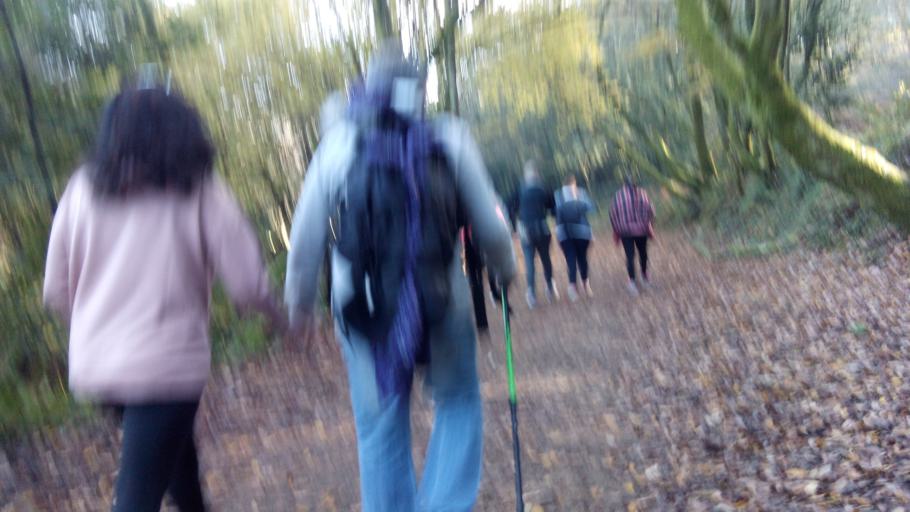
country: ES
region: Galicia
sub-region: Provincia de Pontevedra
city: Meis
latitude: 42.4860
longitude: -8.7482
